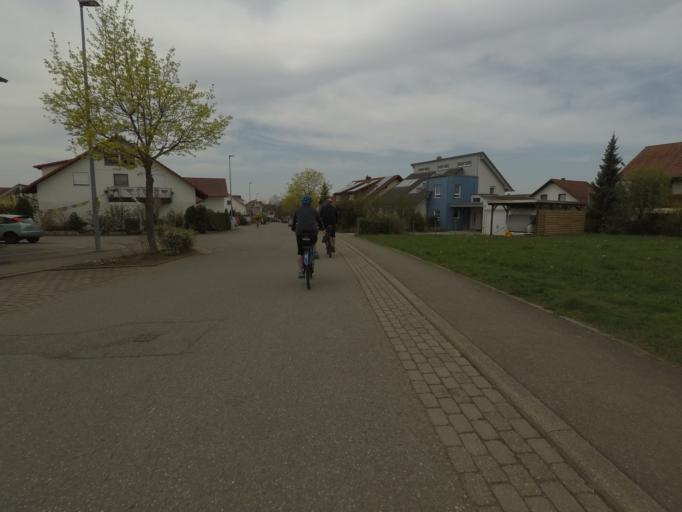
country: DE
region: Baden-Wuerttemberg
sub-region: Tuebingen Region
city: Gomaringen
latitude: 48.4478
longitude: 9.0975
